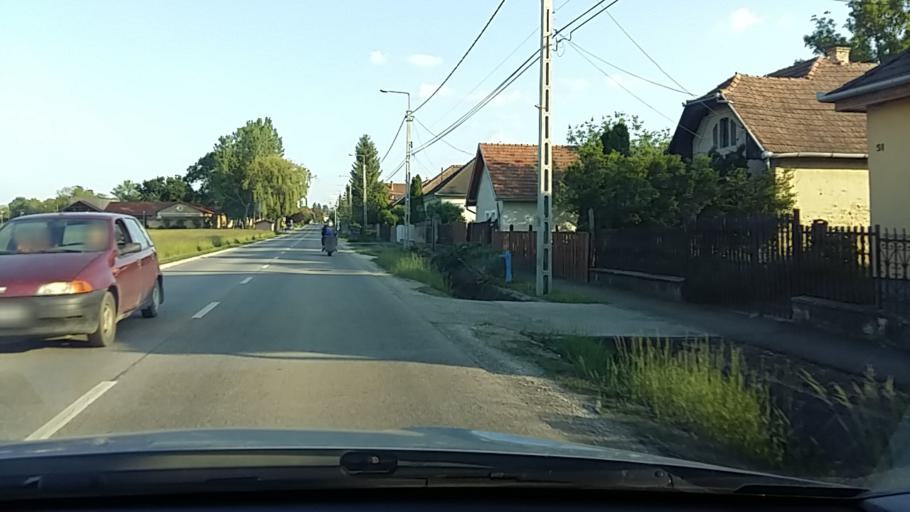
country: HU
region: Pest
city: Orbottyan
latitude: 47.7153
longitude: 19.2331
